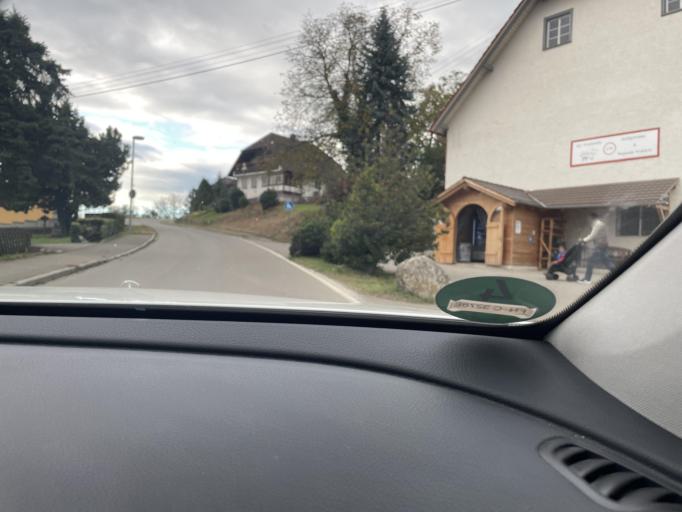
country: DE
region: Baden-Wuerttemberg
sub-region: Tuebingen Region
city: Markdorf
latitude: 47.7280
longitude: 9.3950
